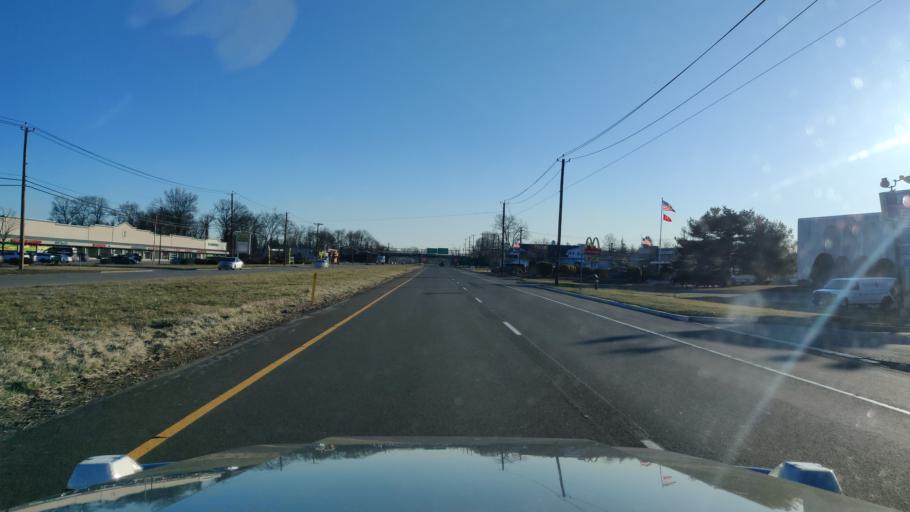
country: US
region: New Jersey
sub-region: Essex County
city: Fairfield
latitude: 40.8841
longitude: -74.2871
